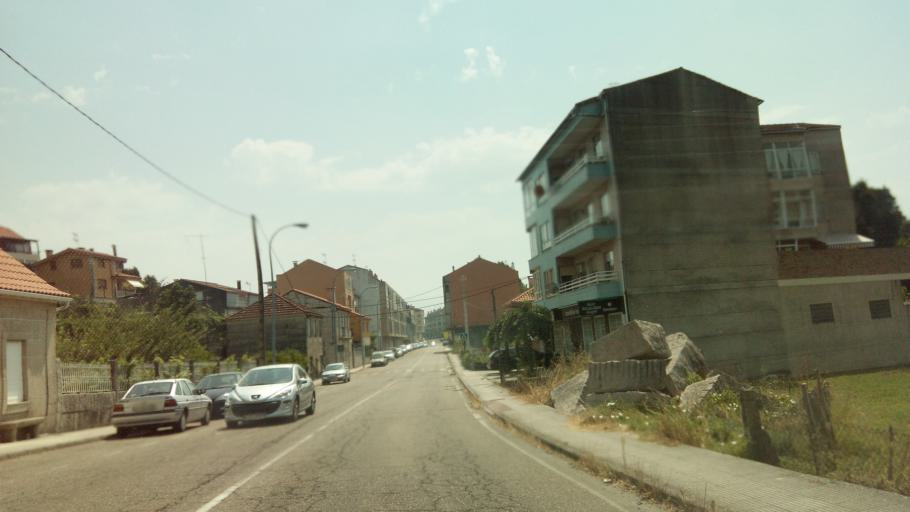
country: ES
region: Galicia
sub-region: Provincia de Pontevedra
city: Tui
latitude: 42.0546
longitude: -8.6529
